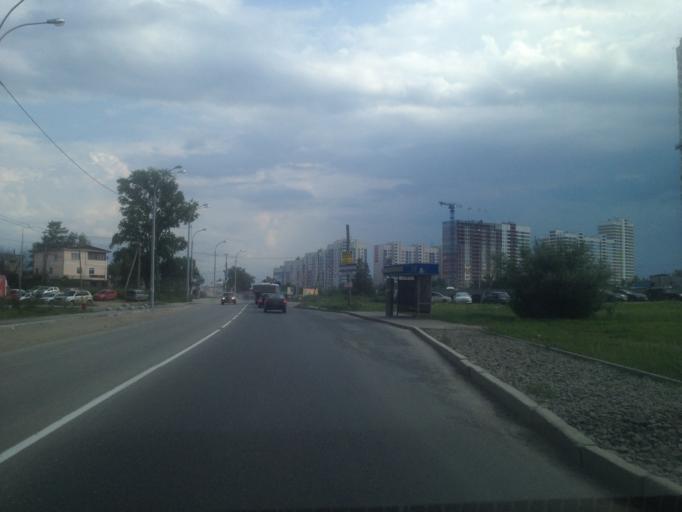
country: RU
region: Sverdlovsk
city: Shirokaya Rechka
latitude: 56.8011
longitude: 60.4941
